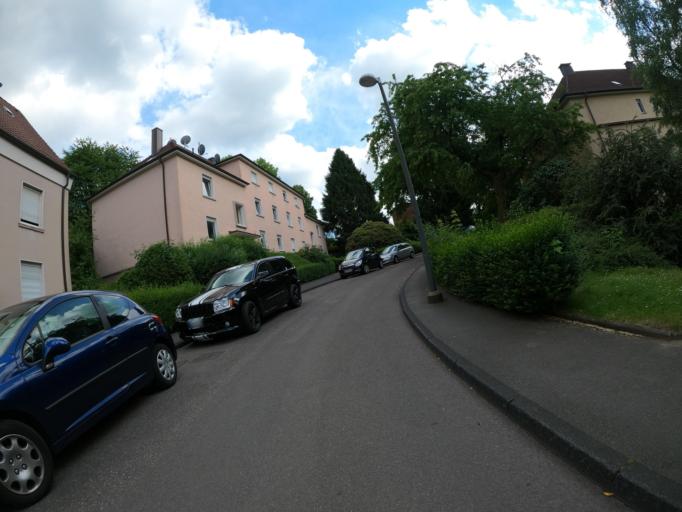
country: DE
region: North Rhine-Westphalia
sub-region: Regierungsbezirk Dusseldorf
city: Wuppertal
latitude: 51.2527
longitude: 7.1128
